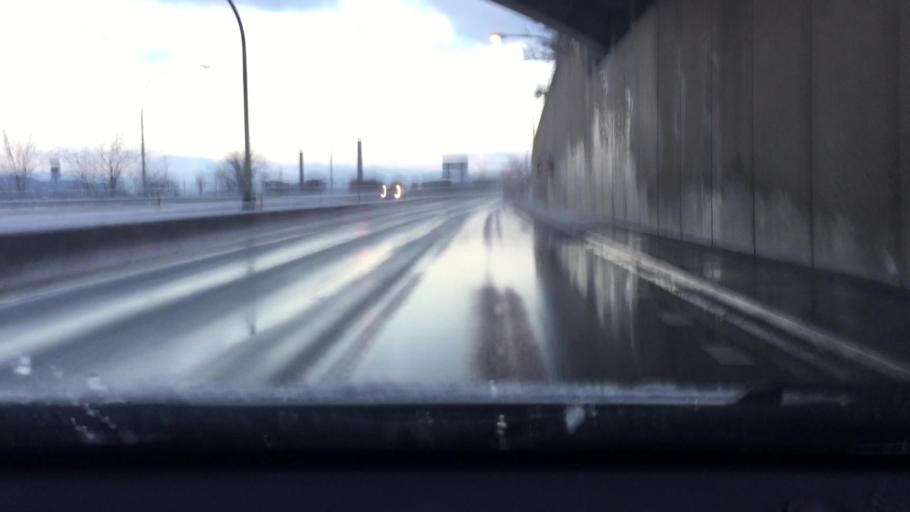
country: US
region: Pennsylvania
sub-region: Allegheny County
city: McKees Rocks
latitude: 40.4666
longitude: -80.0346
